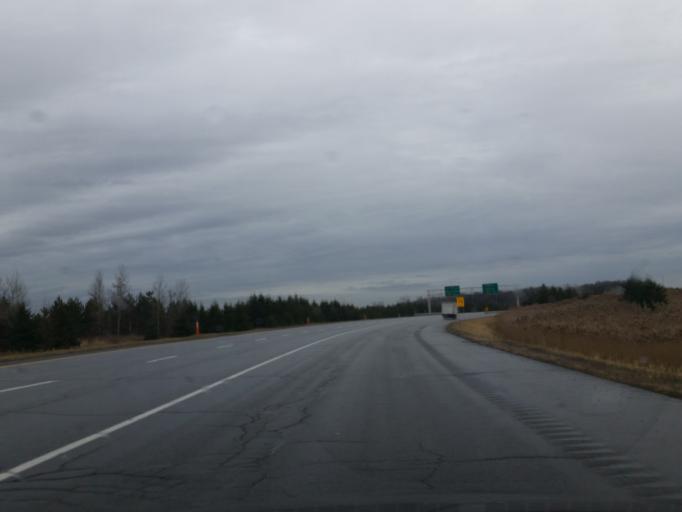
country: CA
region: Quebec
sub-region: Laurentides
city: Saint-Jerome
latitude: 45.7168
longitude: -73.9821
